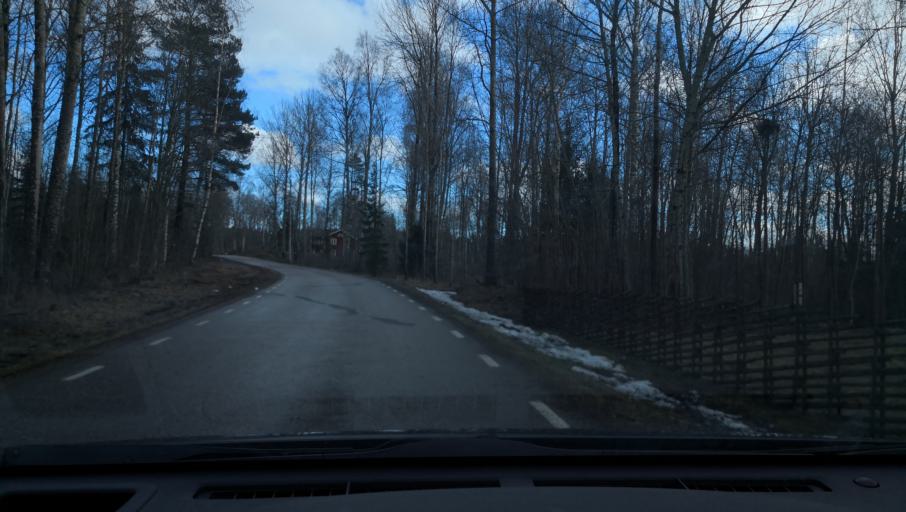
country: SE
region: OErebro
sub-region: Lindesbergs Kommun
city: Fellingsbro
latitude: 59.3412
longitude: 15.6886
